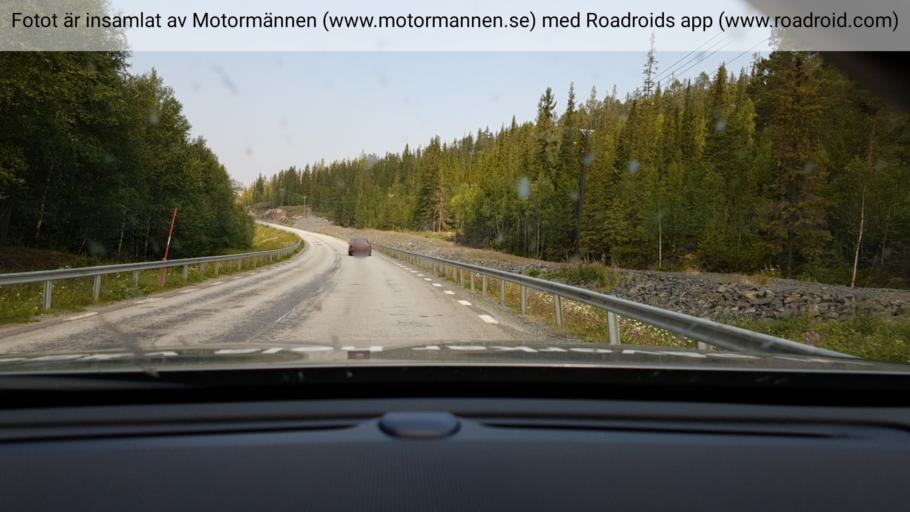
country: SE
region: Vaesterbotten
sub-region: Vilhelmina Kommun
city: Sjoberg
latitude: 65.5291
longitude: 15.6194
